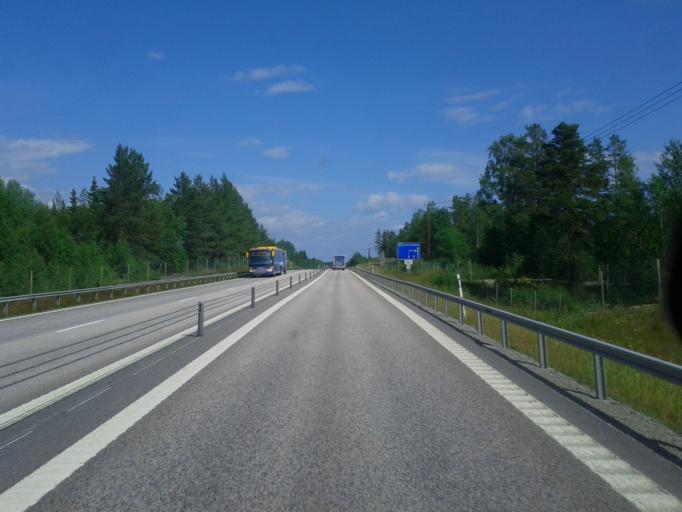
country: SE
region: Vaesterbotten
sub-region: Nordmalings Kommun
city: Nordmaling
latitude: 63.4897
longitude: 19.3130
